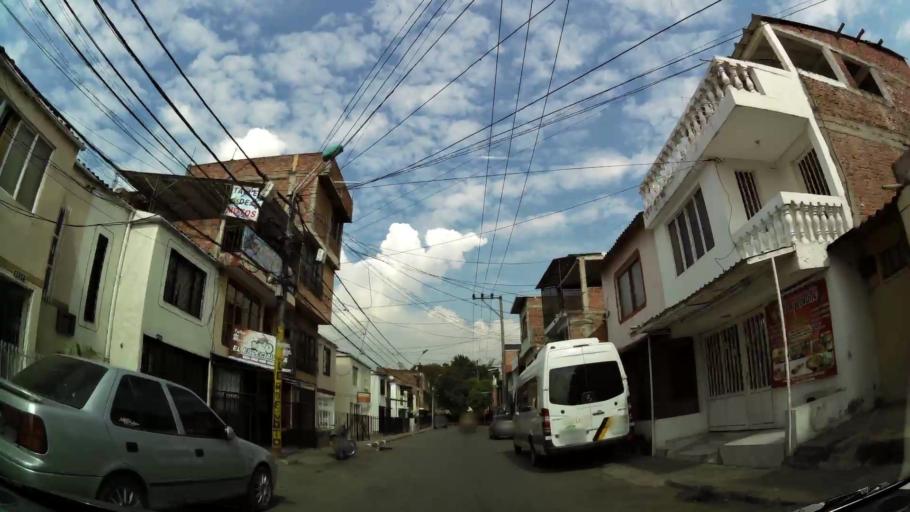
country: CO
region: Valle del Cauca
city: Cali
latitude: 3.4970
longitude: -76.4962
